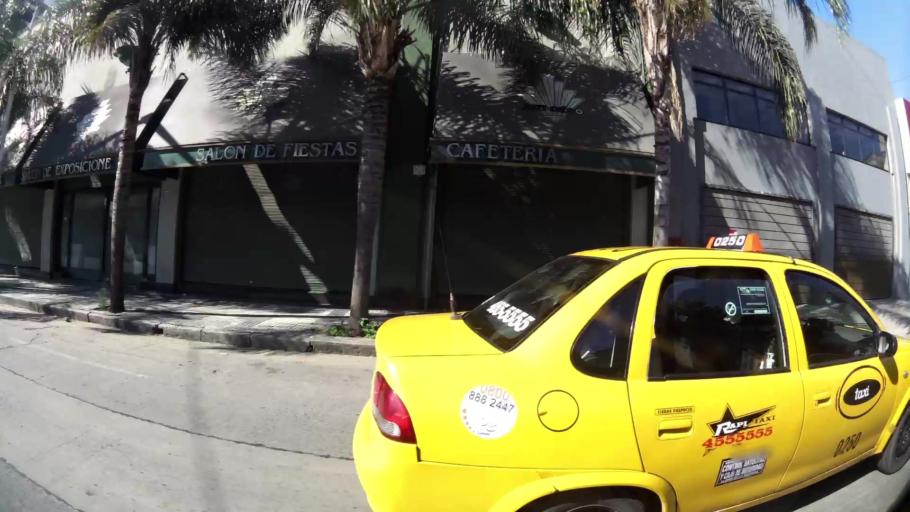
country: AR
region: Cordoba
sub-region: Departamento de Capital
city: Cordoba
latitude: -31.4085
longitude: -64.1875
